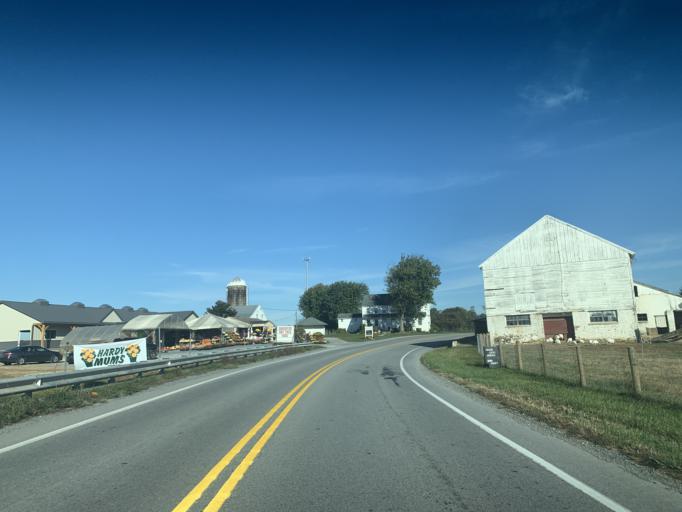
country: US
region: Pennsylvania
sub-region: Chester County
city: Parkesburg
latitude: 39.9188
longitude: -75.9142
